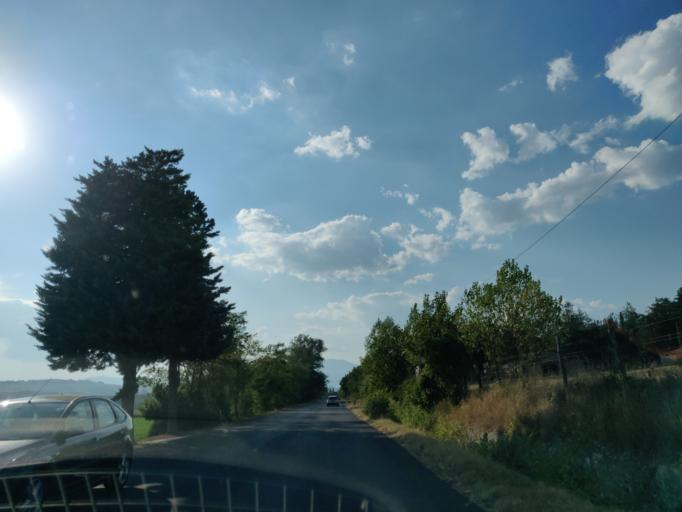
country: IT
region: Latium
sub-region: Provincia di Viterbo
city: Proceno
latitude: 42.7762
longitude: 11.8433
